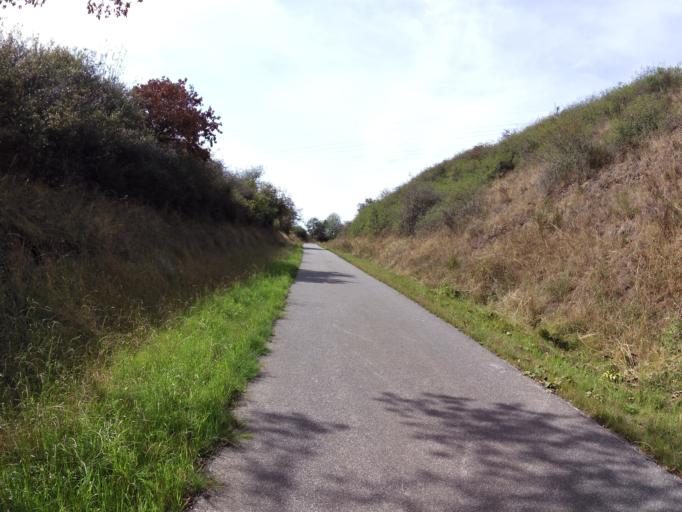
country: DE
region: Rheinland-Pfalz
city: Lichtenborn
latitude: 50.1150
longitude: 6.2744
